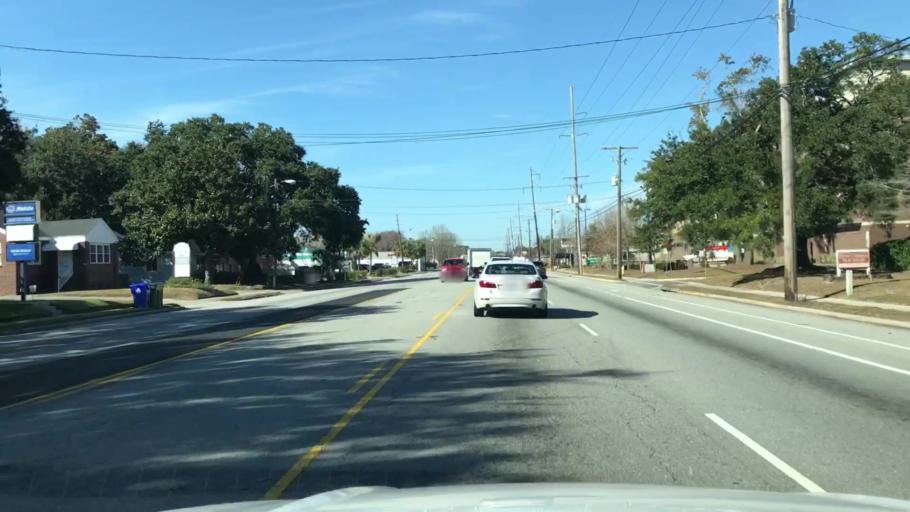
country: US
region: South Carolina
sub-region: Charleston County
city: Charleston
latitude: 32.7897
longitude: -79.9852
